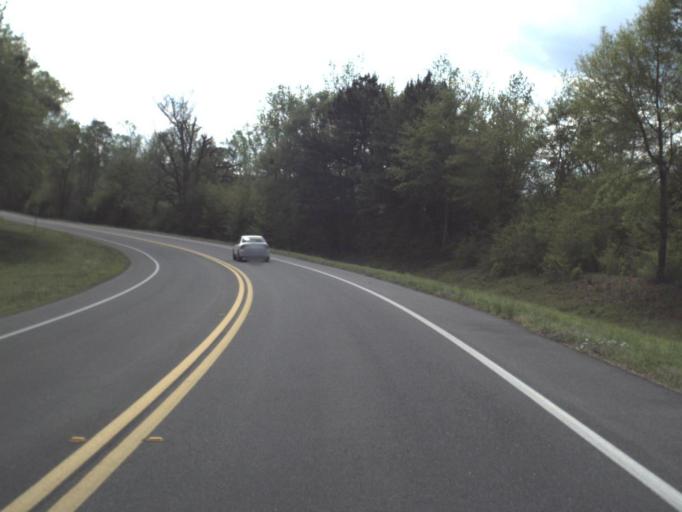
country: US
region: Alabama
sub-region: Covington County
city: Florala
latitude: 30.9708
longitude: -86.4529
